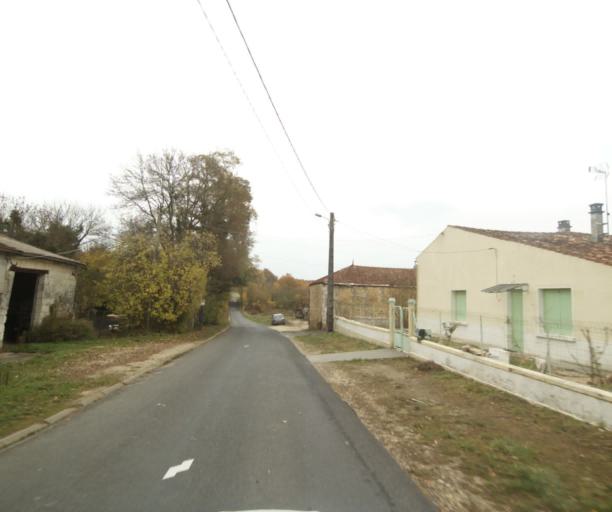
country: FR
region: Poitou-Charentes
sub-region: Departement de la Charente-Maritime
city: Chermignac
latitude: 45.7110
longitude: -0.6931
